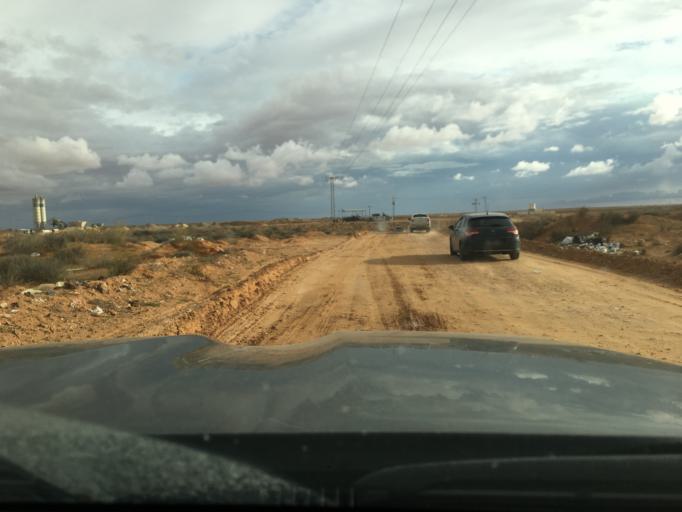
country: TN
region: Madanin
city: Medenine
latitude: 33.2696
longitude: 10.5685
